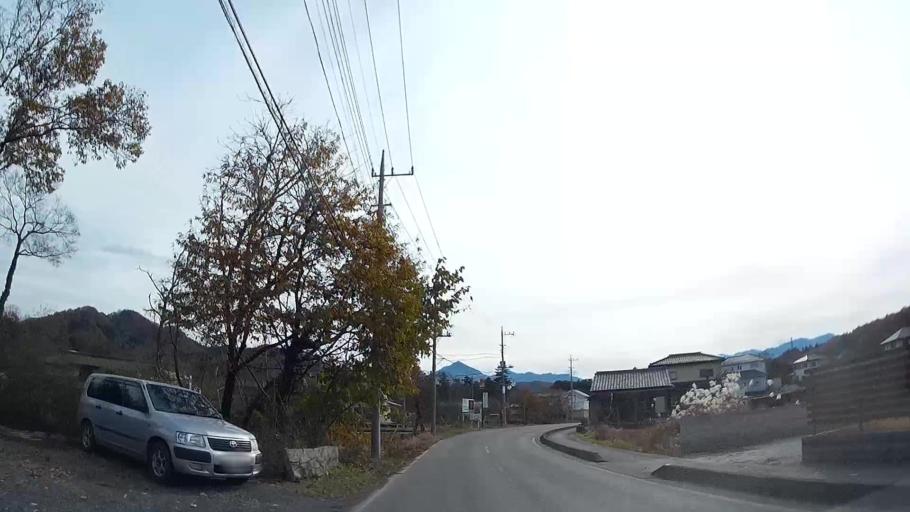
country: JP
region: Saitama
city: Chichibu
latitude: 36.0284
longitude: 139.0375
